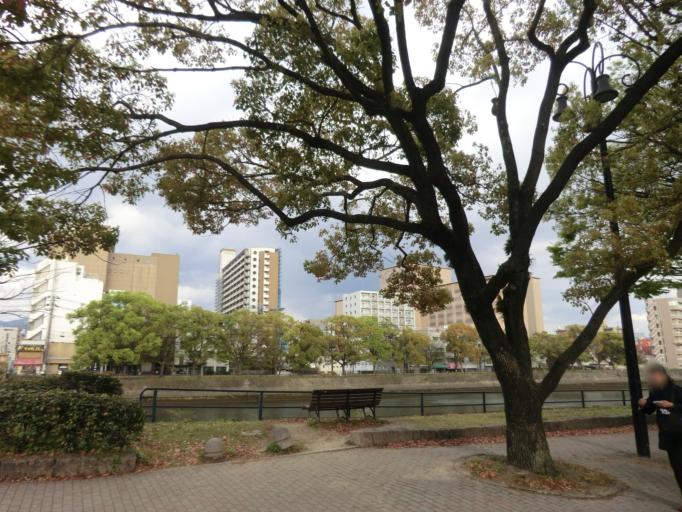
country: JP
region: Hiroshima
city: Hiroshima-shi
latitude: 34.3932
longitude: 132.4752
